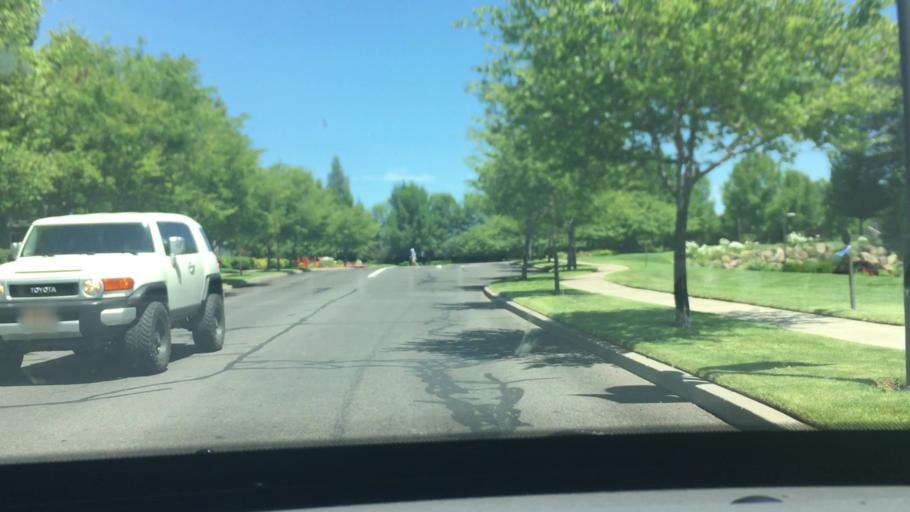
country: US
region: Oregon
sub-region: Deschutes County
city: Bend
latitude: 44.0481
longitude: -121.3146
